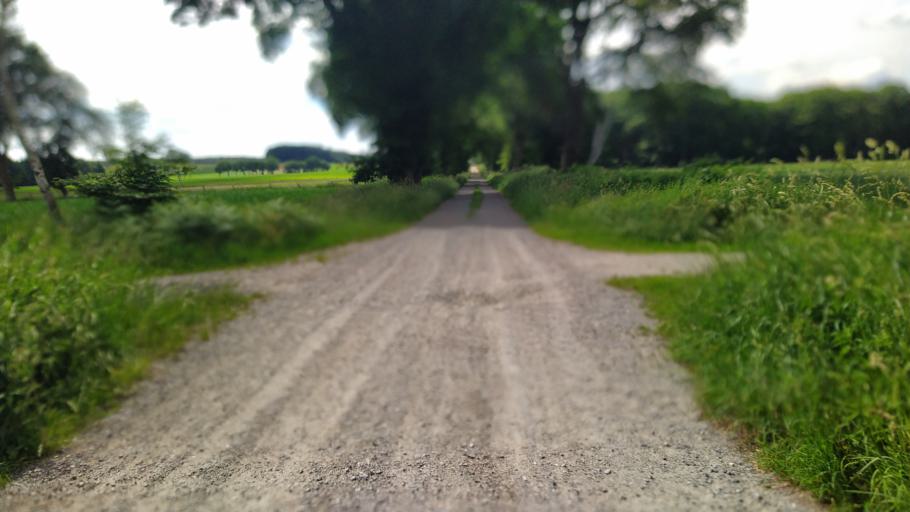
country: DE
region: Lower Saxony
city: Armstorf
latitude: 53.6045
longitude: 9.0696
